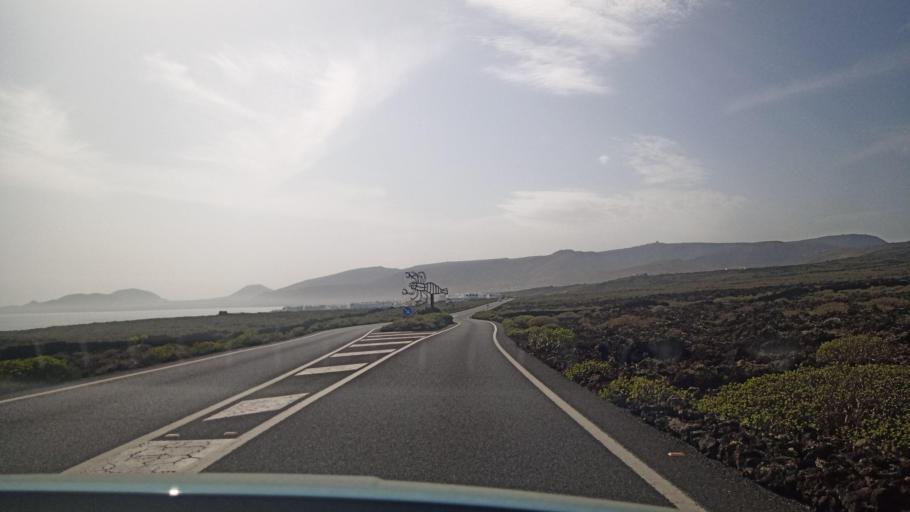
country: ES
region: Canary Islands
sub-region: Provincia de Las Palmas
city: Haria
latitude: 29.1540
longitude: -13.4391
